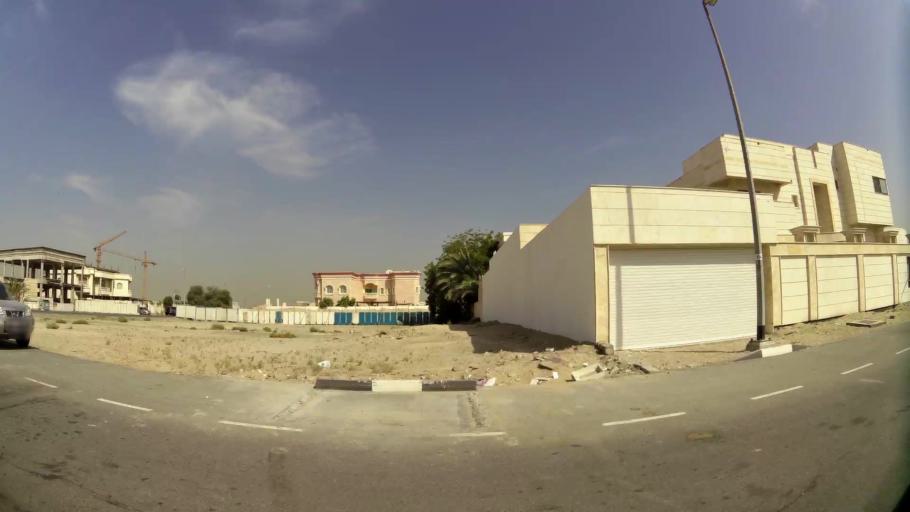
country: AE
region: Ash Shariqah
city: Sharjah
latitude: 25.2784
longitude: 55.3982
